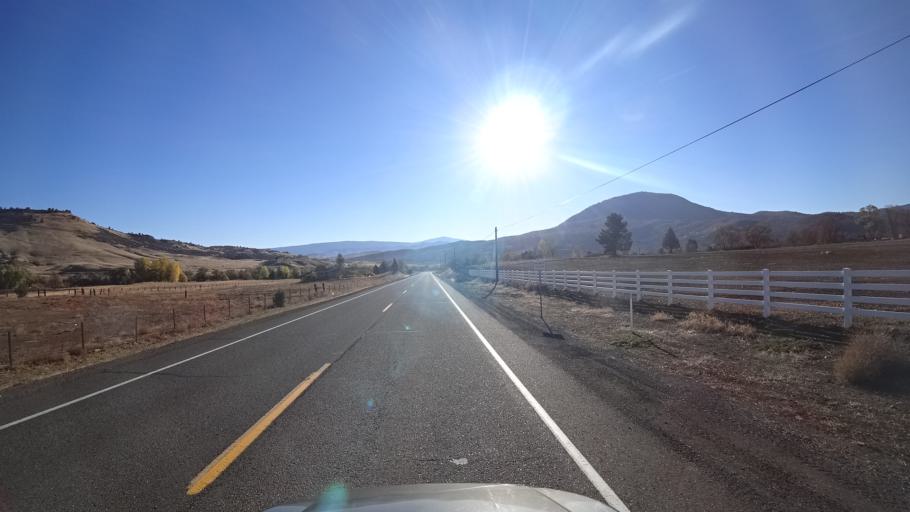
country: US
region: California
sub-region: Siskiyou County
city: Montague
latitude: 41.8993
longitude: -122.5563
